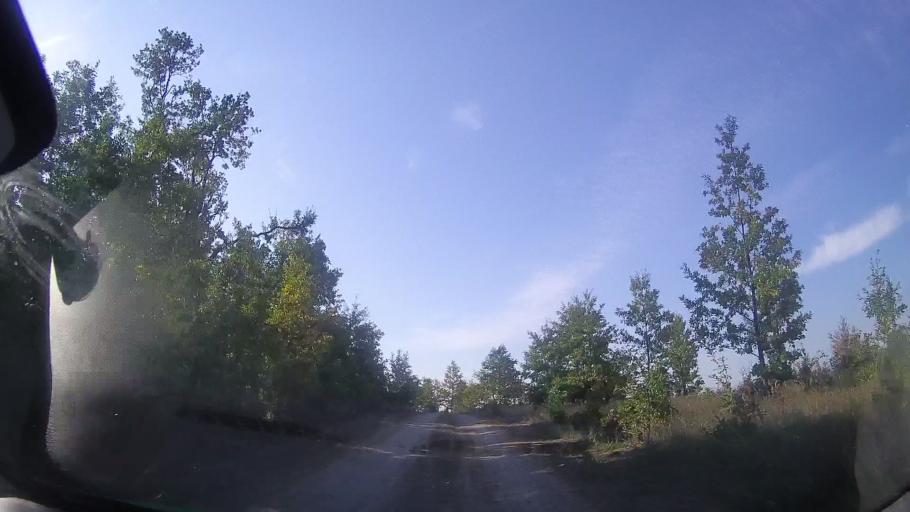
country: RO
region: Timis
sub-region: Comuna Bogda
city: Bogda
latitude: 45.9202
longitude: 21.6119
